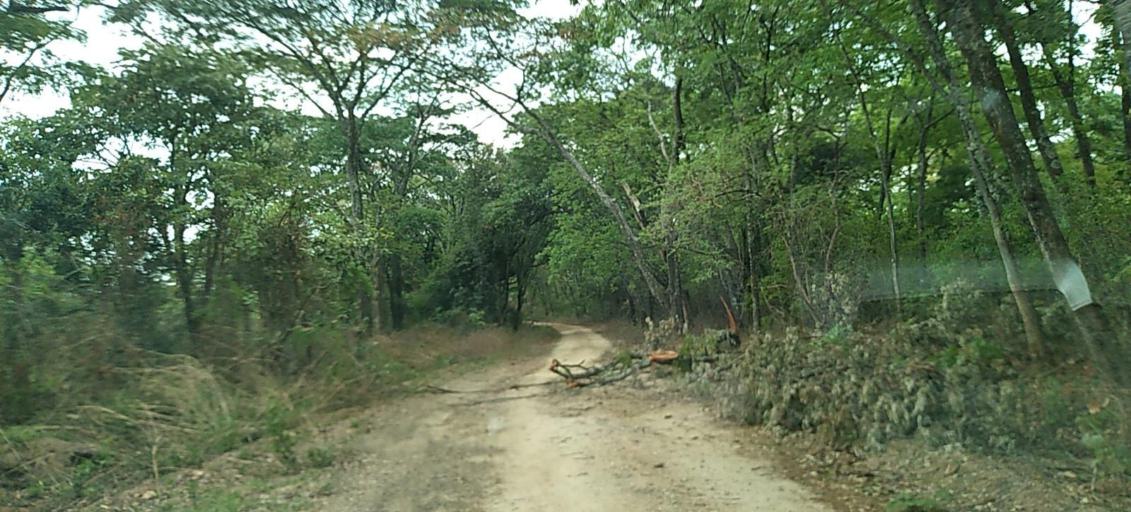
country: ZM
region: Copperbelt
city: Chingola
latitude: -12.7511
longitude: 27.7247
